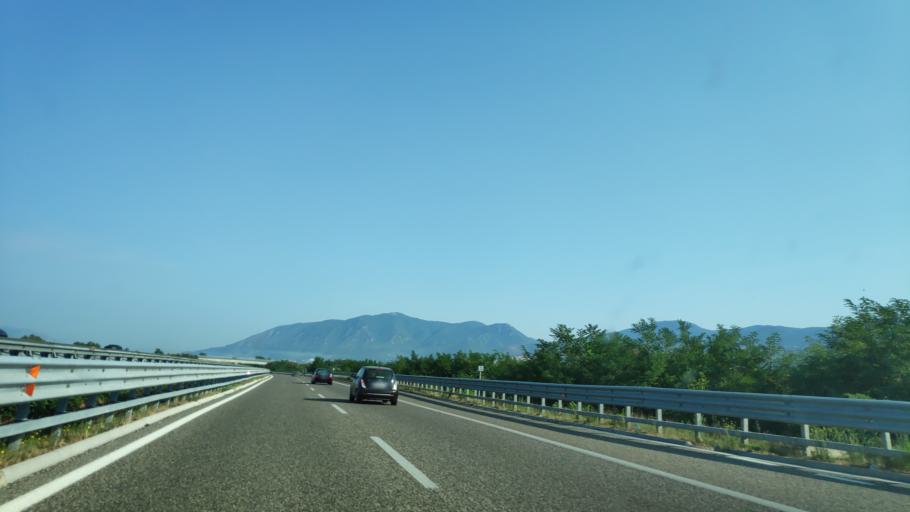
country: IT
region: Campania
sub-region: Provincia di Salerno
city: Padula
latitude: 40.3214
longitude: 15.6381
